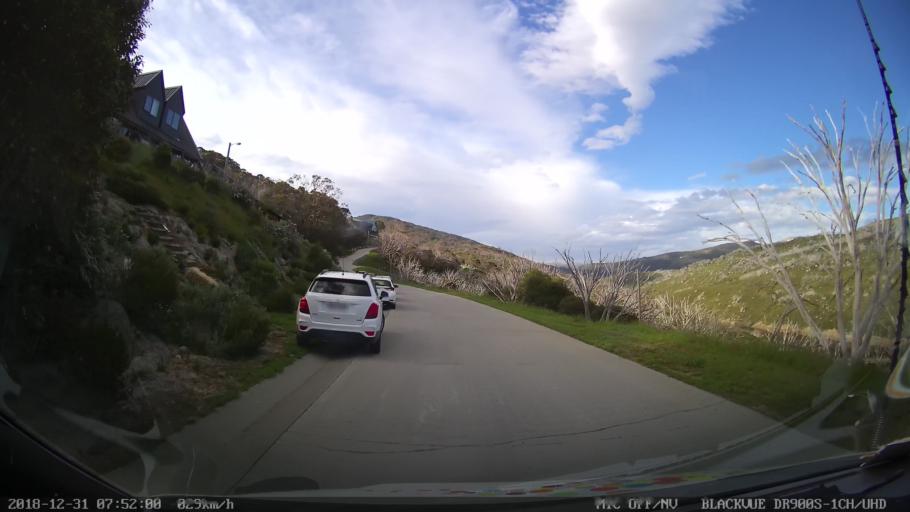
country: AU
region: New South Wales
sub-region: Snowy River
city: Jindabyne
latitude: -36.3788
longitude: 148.3740
